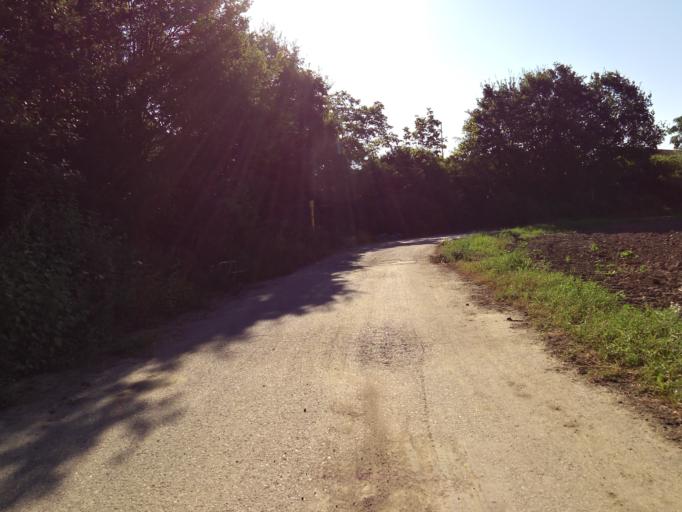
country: DE
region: Rheinland-Pfalz
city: Gartenstadt
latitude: 49.4834
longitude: 8.4121
